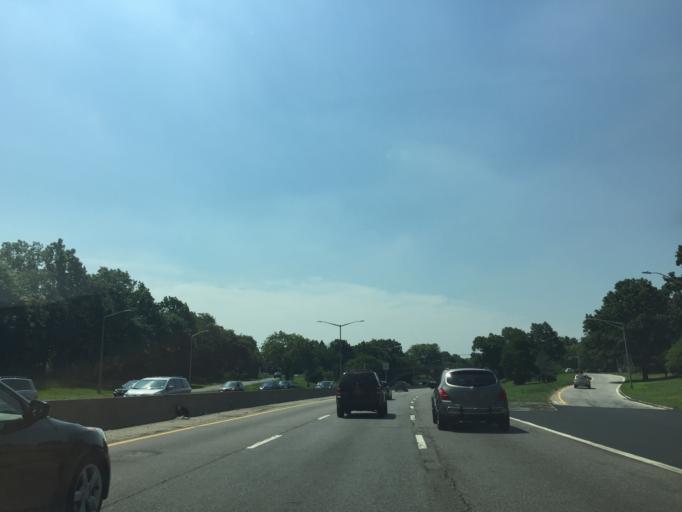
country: US
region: New York
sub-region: Nassau County
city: Bellerose
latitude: 40.7364
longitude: -73.7233
